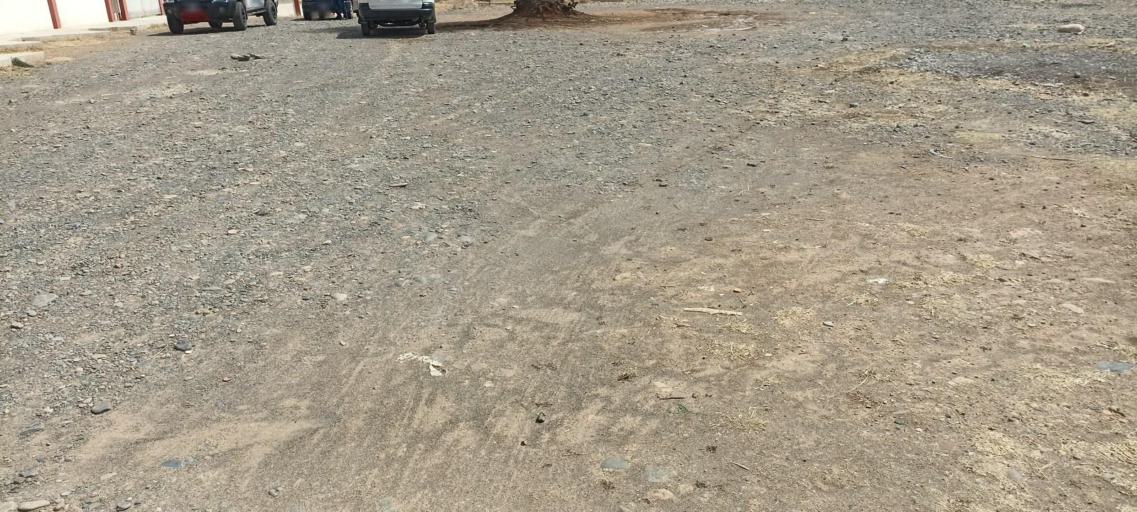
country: BO
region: La Paz
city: Batallas
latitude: -16.4018
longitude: -68.4800
